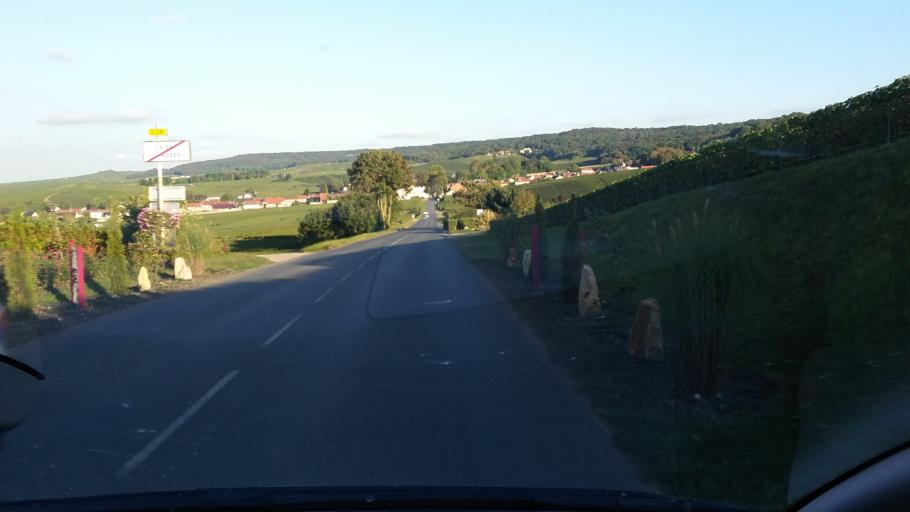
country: FR
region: Champagne-Ardenne
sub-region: Departement de la Marne
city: Rilly-la-Montagne
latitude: 49.1573
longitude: 4.0674
